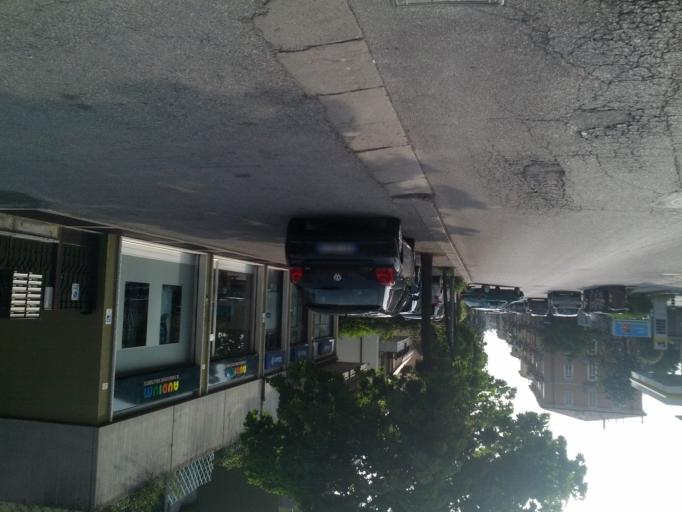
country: IT
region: Veneto
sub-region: Provincia di Verona
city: Poiano
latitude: 45.4401
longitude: 11.0262
